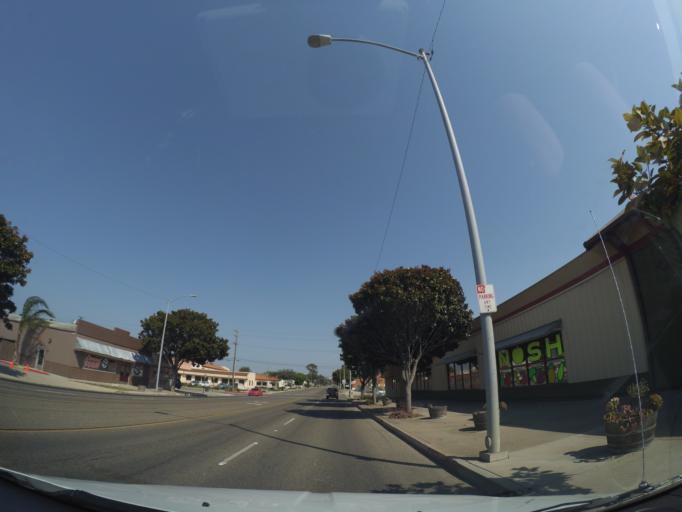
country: US
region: California
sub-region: Santa Barbara County
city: Lompoc
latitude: 34.6389
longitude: -120.4548
